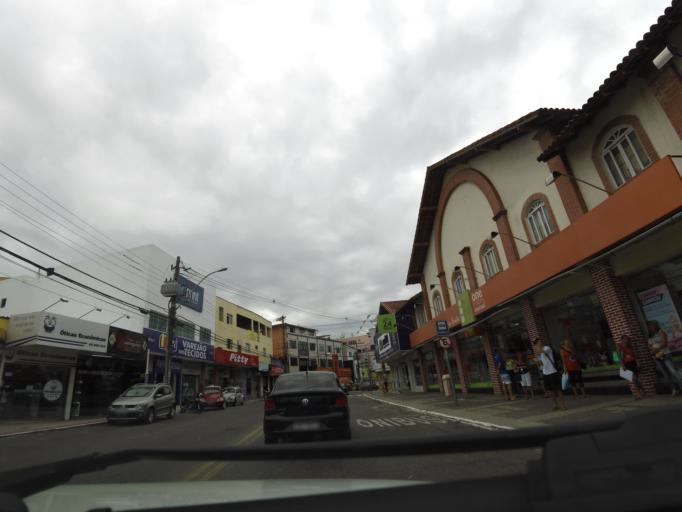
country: BR
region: Espirito Santo
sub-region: Guarapari
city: Guarapari
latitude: -20.6668
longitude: -40.4702
